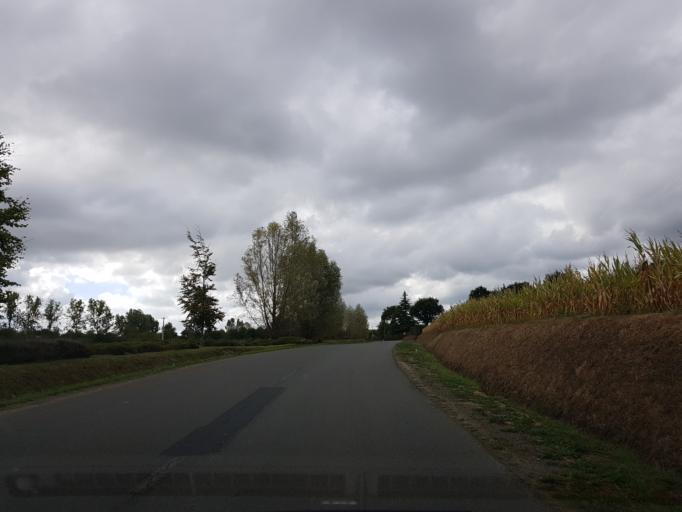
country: FR
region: Brittany
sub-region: Departement des Cotes-d'Armor
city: Quessoy
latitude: 48.4445
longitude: -2.6479
